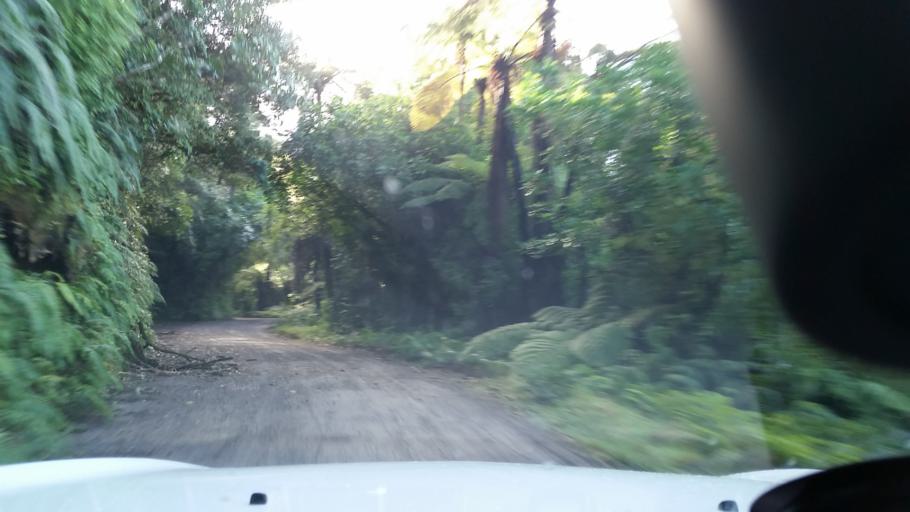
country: NZ
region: Bay of Plenty
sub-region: Kawerau District
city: Kawerau
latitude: -38.0195
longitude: 176.5936
